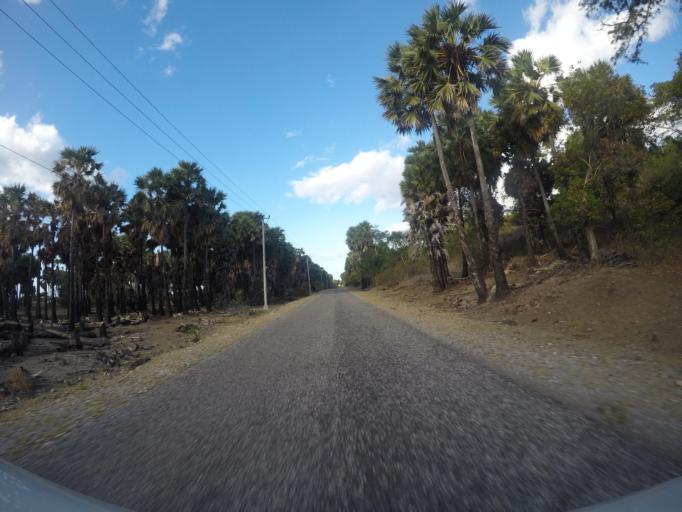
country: TL
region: Lautem
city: Lospalos
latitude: -8.3405
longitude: 126.9333
